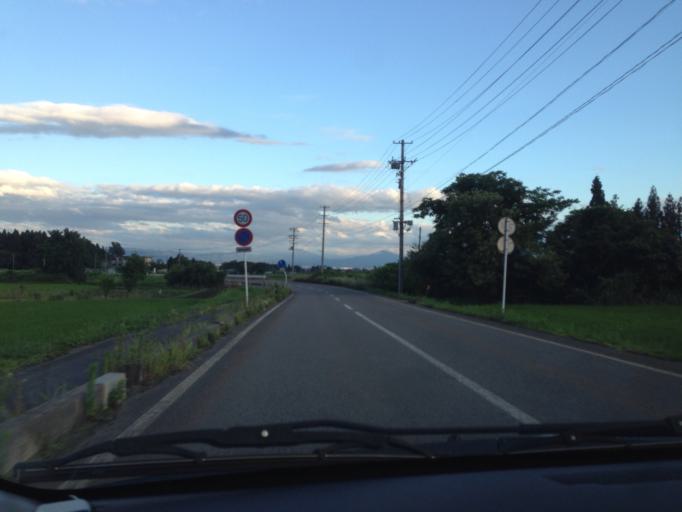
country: JP
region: Fukushima
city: Kitakata
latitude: 37.6866
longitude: 139.8587
